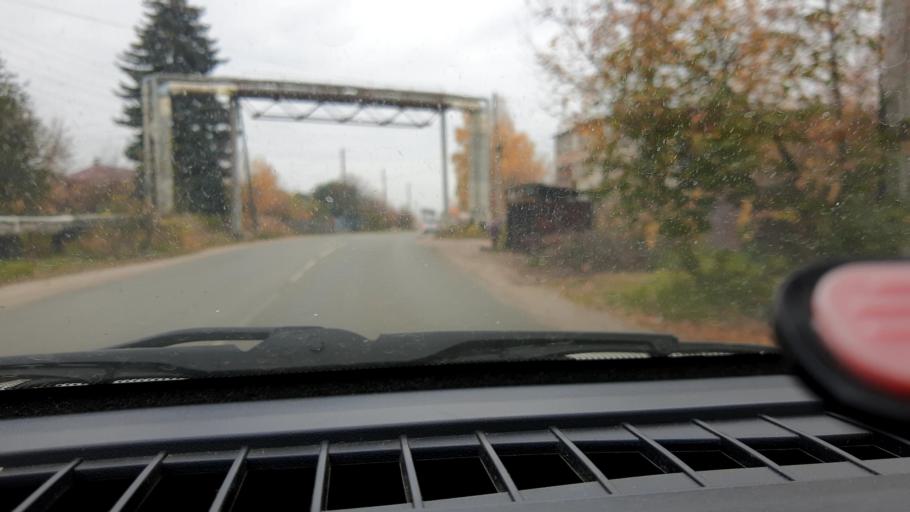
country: RU
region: Nizjnij Novgorod
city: Gorodets
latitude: 56.6454
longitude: 43.4887
